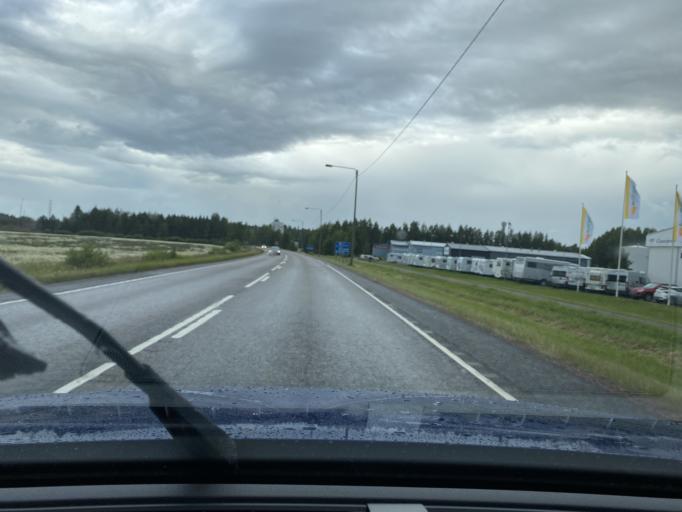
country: FI
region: Uusimaa
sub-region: Helsinki
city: Hyvinge
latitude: 60.6134
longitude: 24.8101
